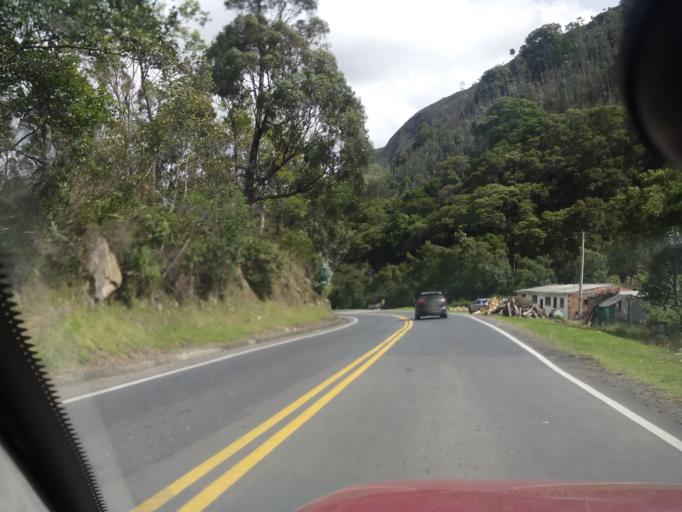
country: CO
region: Boyaca
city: Arcabuco
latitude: 5.7379
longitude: -73.4131
